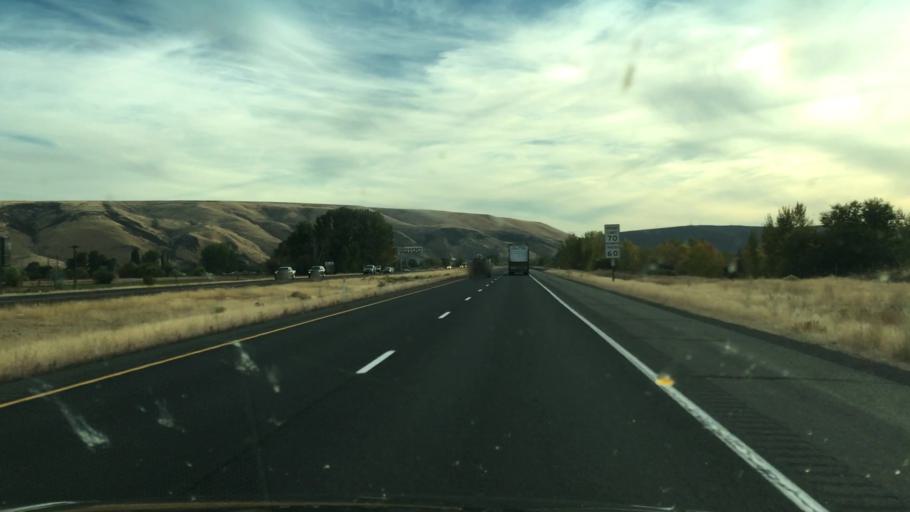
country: US
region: Washington
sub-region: Yakima County
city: Selah
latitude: 46.6684
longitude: -120.4896
